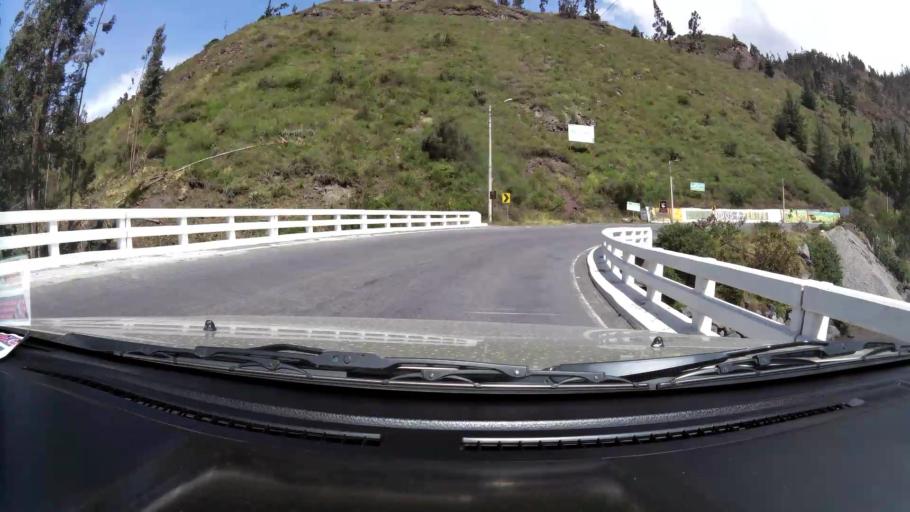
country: EC
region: Chimborazo
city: Guano
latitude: -1.5675
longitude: -78.5352
